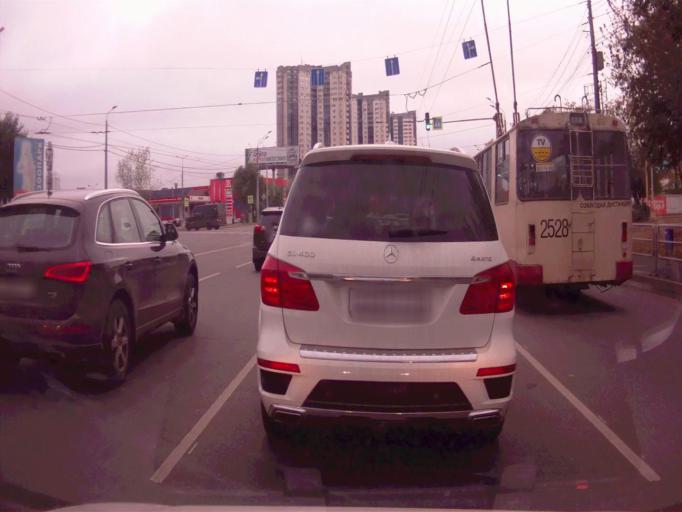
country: RU
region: Chelyabinsk
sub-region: Gorod Chelyabinsk
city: Chelyabinsk
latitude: 55.1707
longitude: 61.3702
